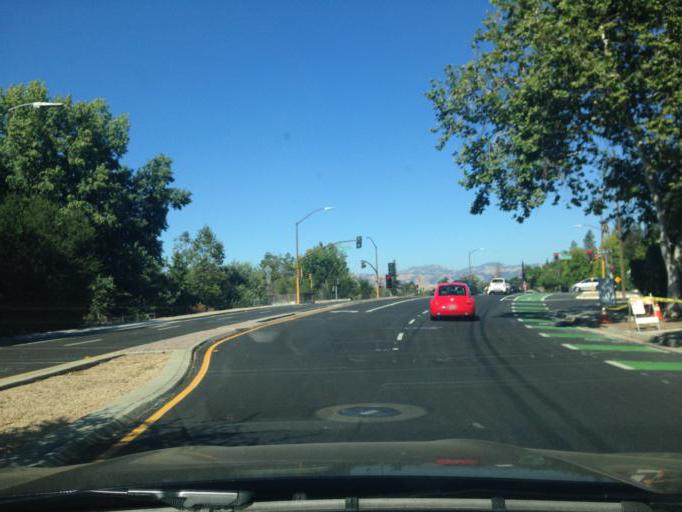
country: US
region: California
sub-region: Santa Clara County
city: Cambrian Park
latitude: 37.2376
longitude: -121.8876
